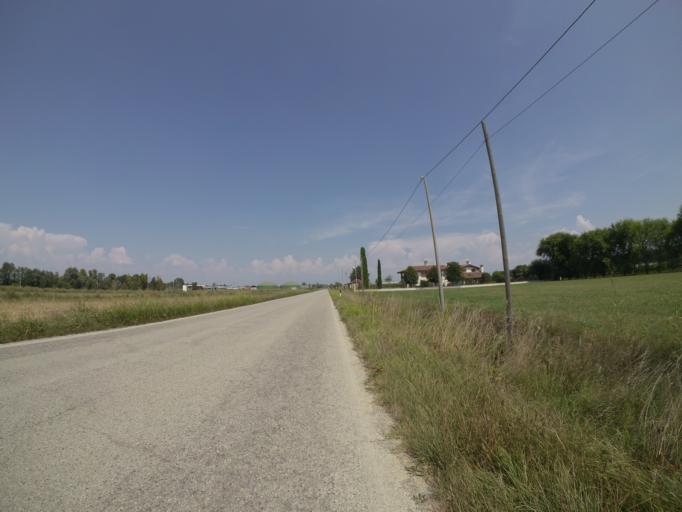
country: IT
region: Friuli Venezia Giulia
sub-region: Provincia di Udine
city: Pocenia
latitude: 45.8567
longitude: 13.1058
